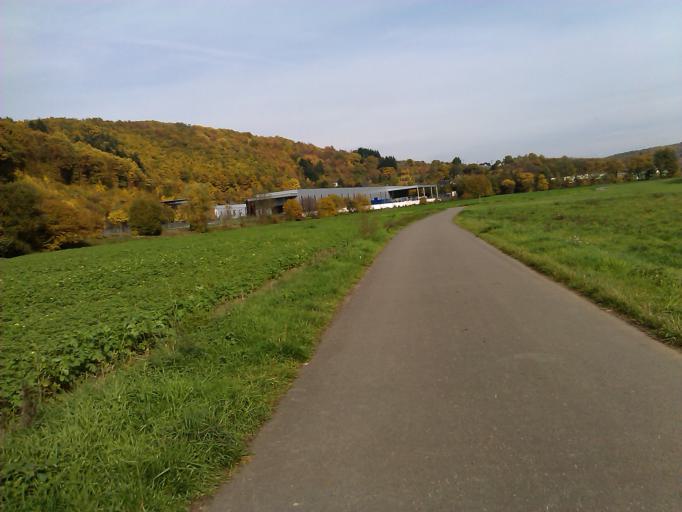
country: DE
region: Rheinland-Pfalz
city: Lauterecken
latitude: 49.6628
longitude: 7.5981
